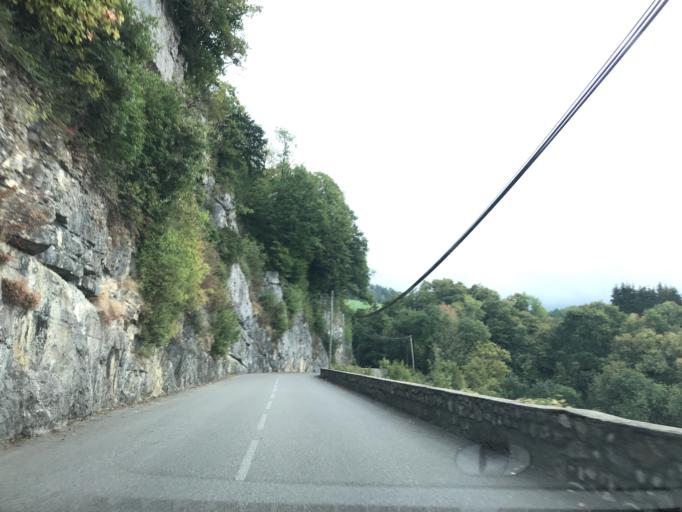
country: FR
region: Rhone-Alpes
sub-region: Departement de la Haute-Savoie
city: Talloires
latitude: 45.8419
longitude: 6.2223
